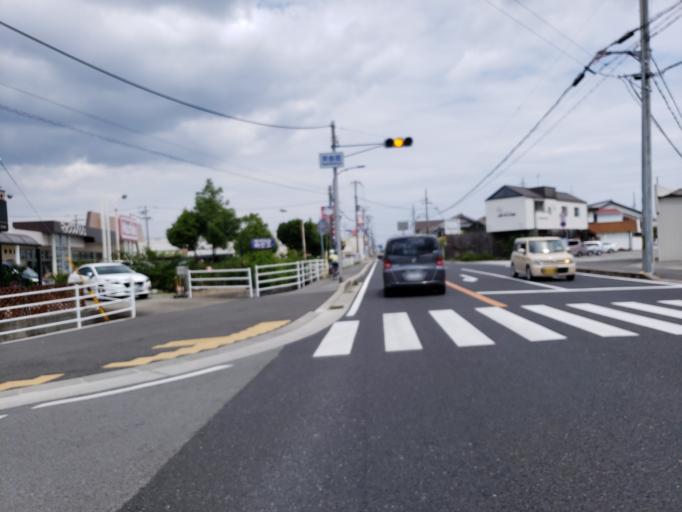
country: JP
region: Hyogo
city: Tatsunocho-tominaga
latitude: 34.7828
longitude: 134.5623
